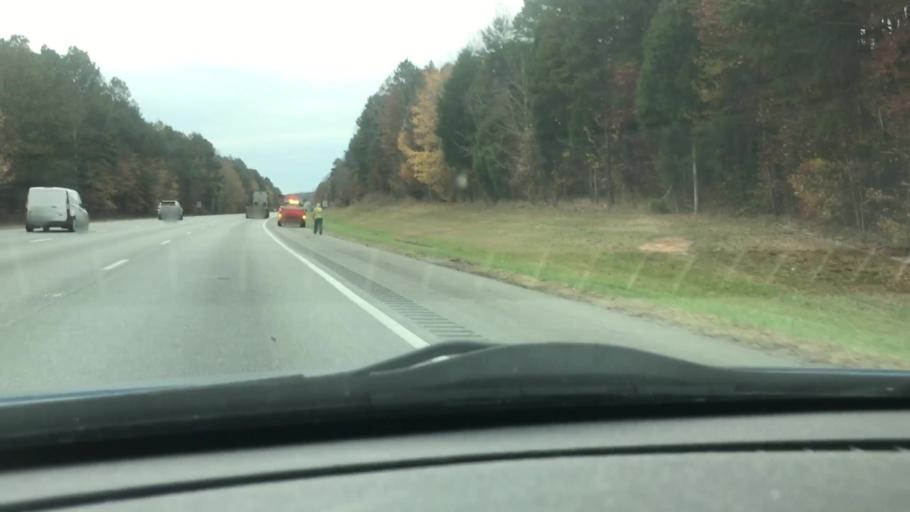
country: US
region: North Carolina
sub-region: Davidson County
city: Lexington
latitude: 35.8047
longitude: -80.1898
